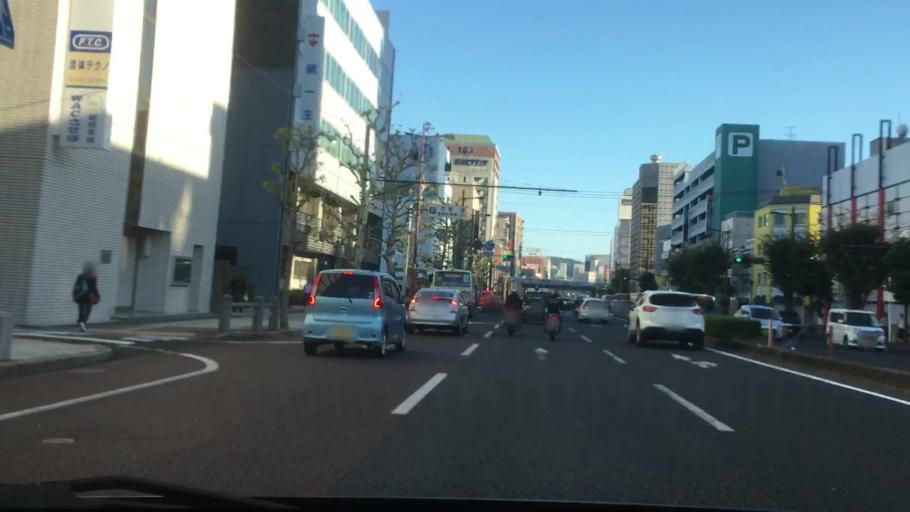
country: JP
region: Nagasaki
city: Sasebo
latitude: 33.1747
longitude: 129.7194
